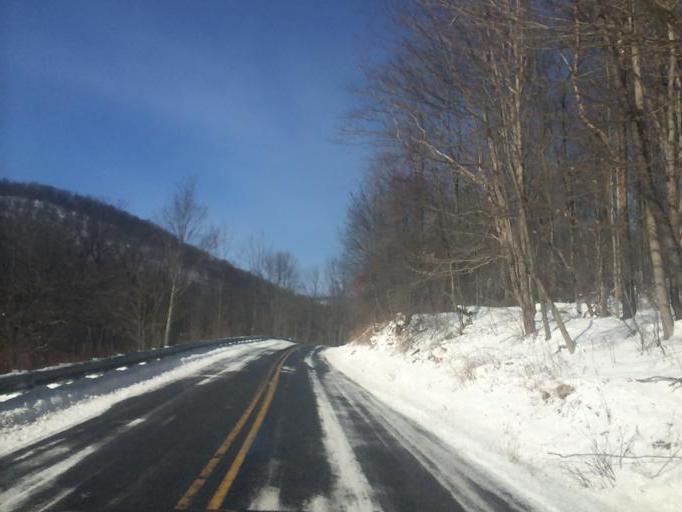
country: US
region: Pennsylvania
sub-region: Centre County
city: Stormstown
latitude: 40.8504
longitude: -78.0080
